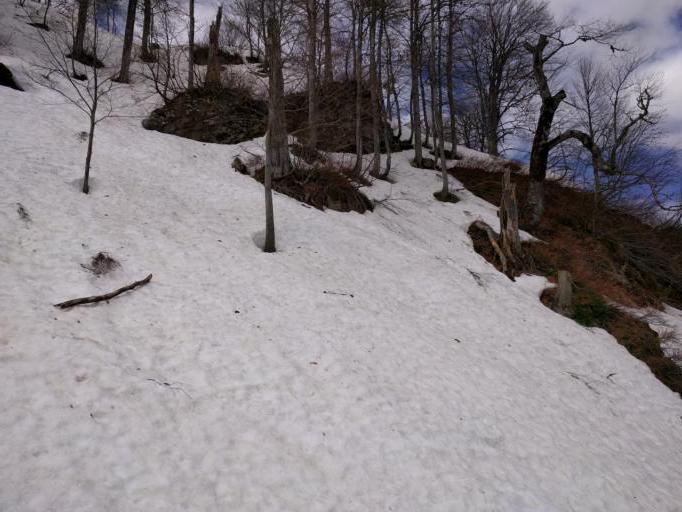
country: RU
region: Krasnodarskiy
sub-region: Sochi City
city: Krasnaya Polyana
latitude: 43.6353
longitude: 40.3126
